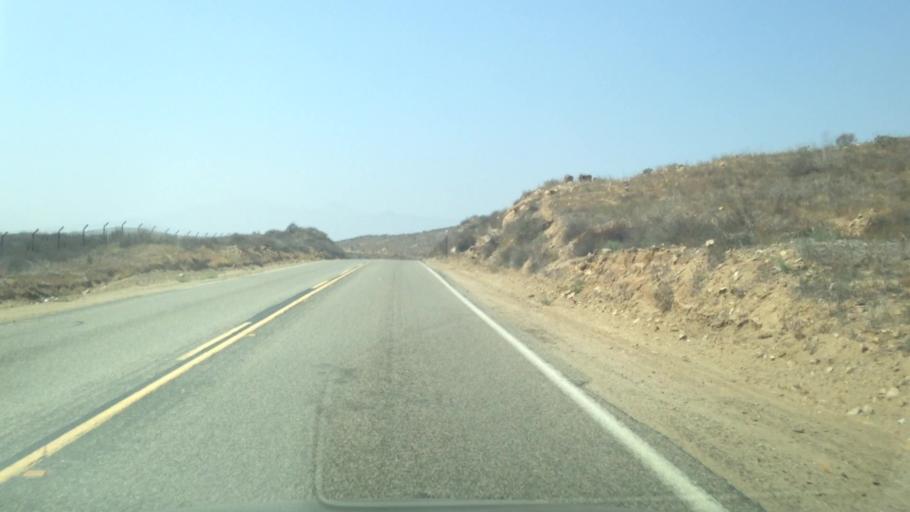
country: US
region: California
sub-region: Riverside County
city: El Cerrito
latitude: 33.8469
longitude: -117.4622
